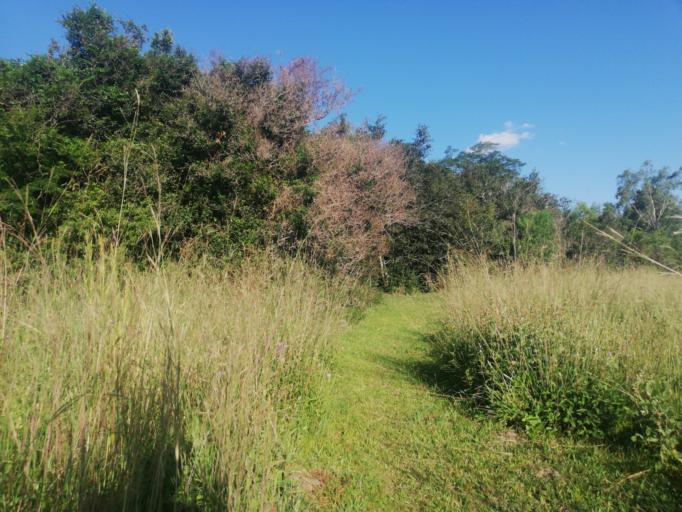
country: AR
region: Corrientes
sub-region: Departamento de San Miguel
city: San Miguel
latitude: -27.9892
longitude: -57.5408
